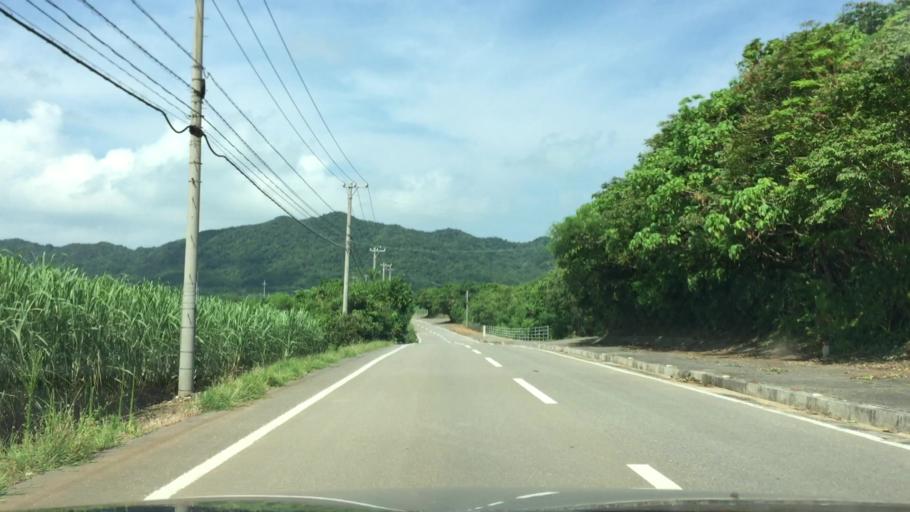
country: JP
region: Okinawa
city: Ishigaki
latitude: 24.4992
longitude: 124.2487
